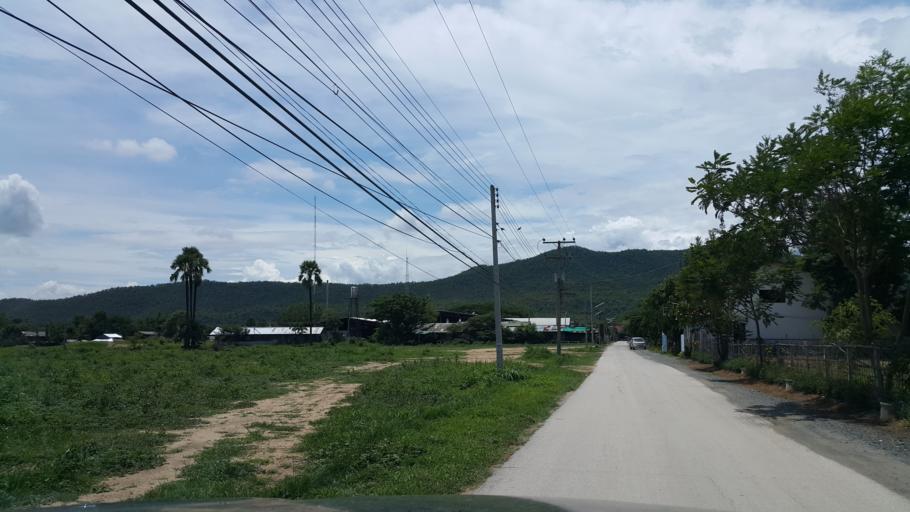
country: TH
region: Chiang Mai
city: Mae On
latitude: 18.7322
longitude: 99.2080
